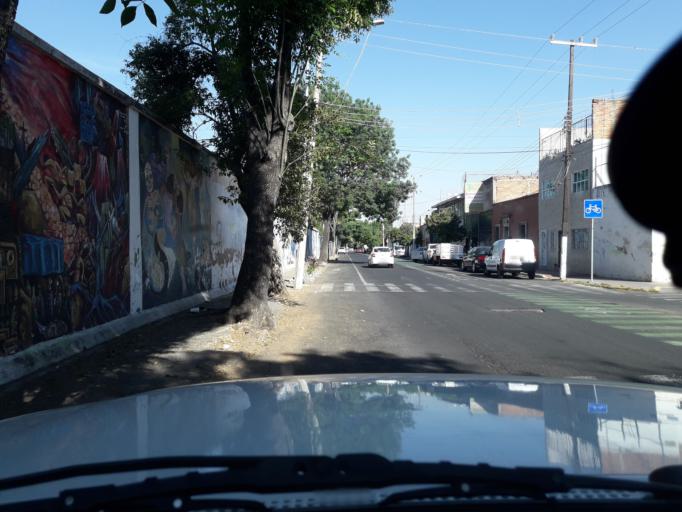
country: MX
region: Jalisco
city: Guadalajara
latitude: 20.6898
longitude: -103.3573
